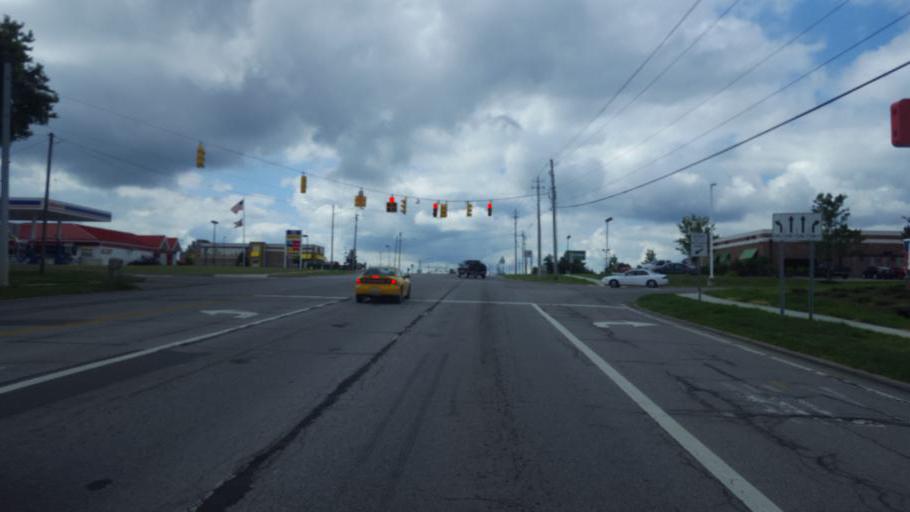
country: US
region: Ohio
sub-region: Richland County
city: Ontario
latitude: 40.7900
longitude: -82.5902
